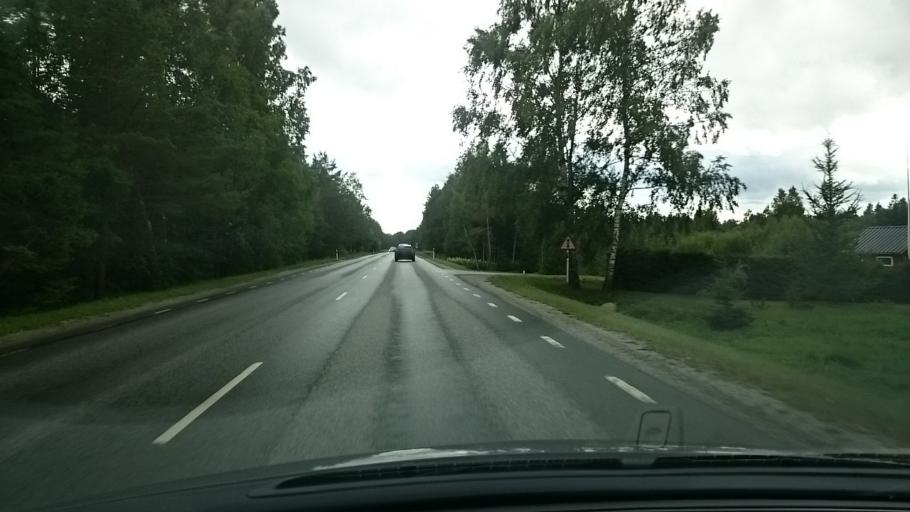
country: EE
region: Harju
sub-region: Keila linn
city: Keila
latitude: 59.2572
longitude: 24.2873
